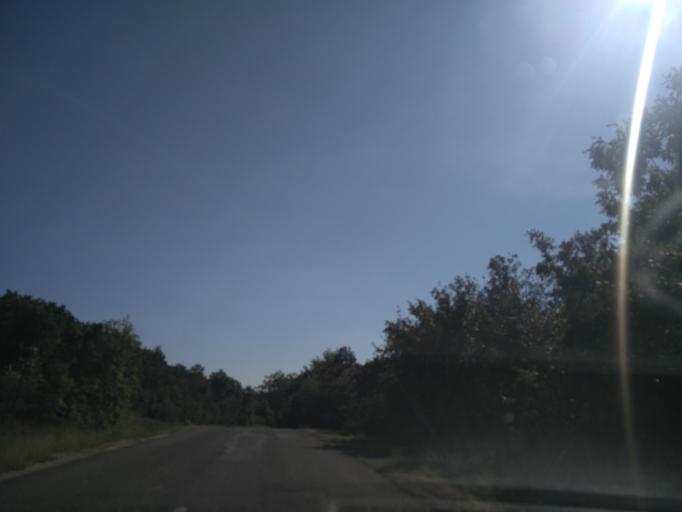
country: HU
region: Fejer
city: Pakozd
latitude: 47.2228
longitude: 18.5788
